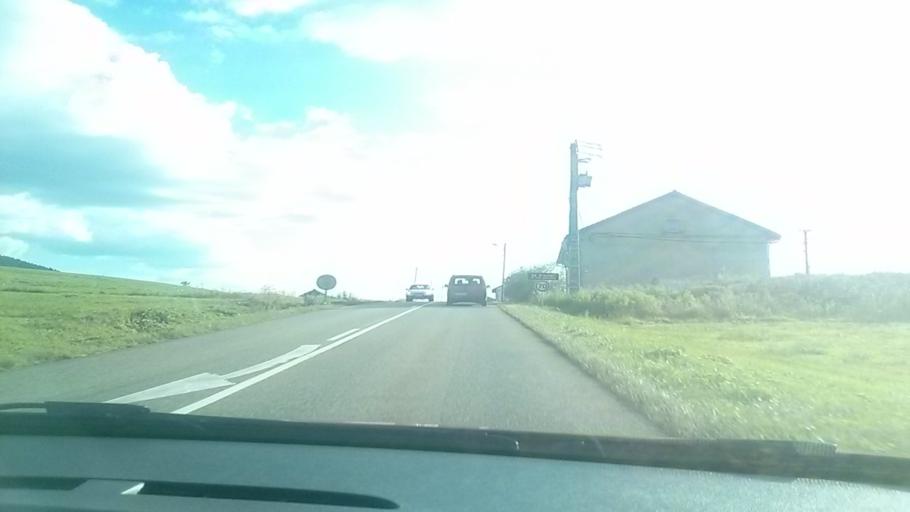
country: FR
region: Franche-Comte
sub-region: Departement du Jura
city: Les Rousses
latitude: 46.5064
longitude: 6.1058
